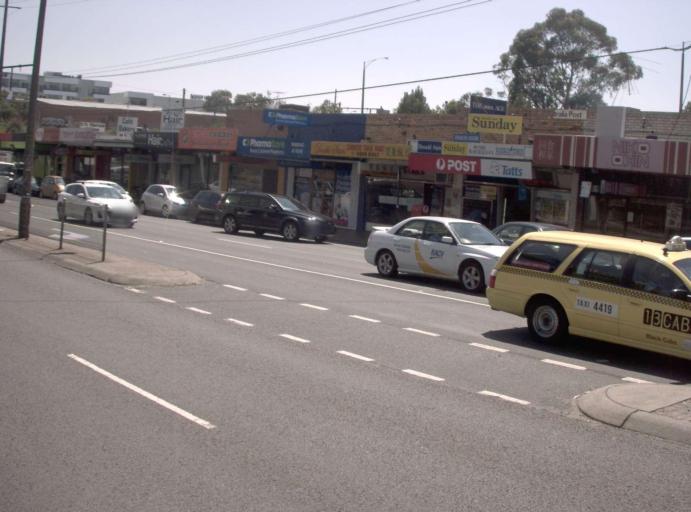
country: AU
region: Victoria
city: Ashburton
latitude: -37.8750
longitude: 145.0916
